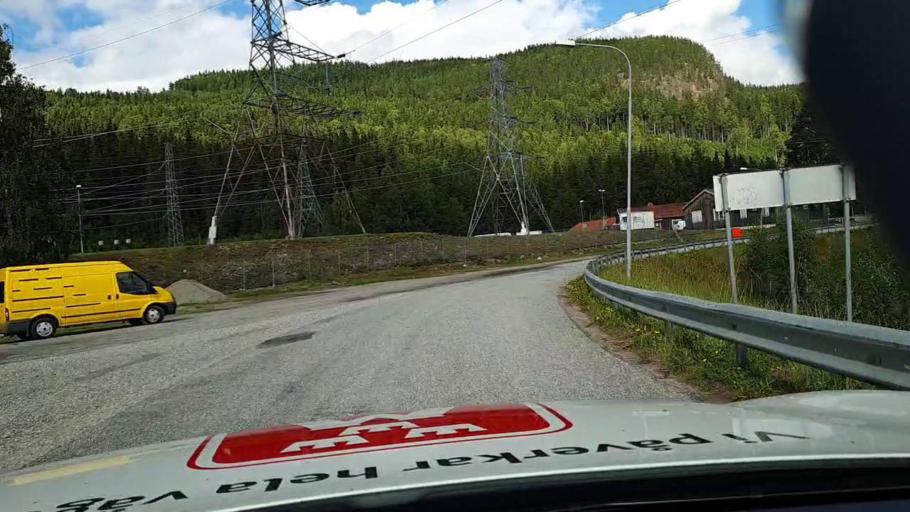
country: SE
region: Jaemtland
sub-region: Ragunda Kommun
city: Hammarstrand
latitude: 63.1466
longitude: 16.0743
